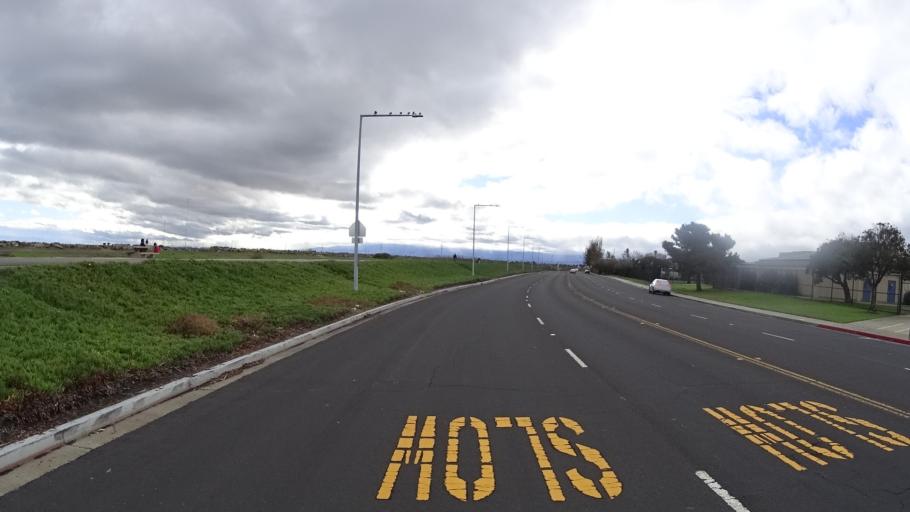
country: US
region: California
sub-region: San Mateo County
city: Foster City
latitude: 37.5601
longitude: -122.2477
